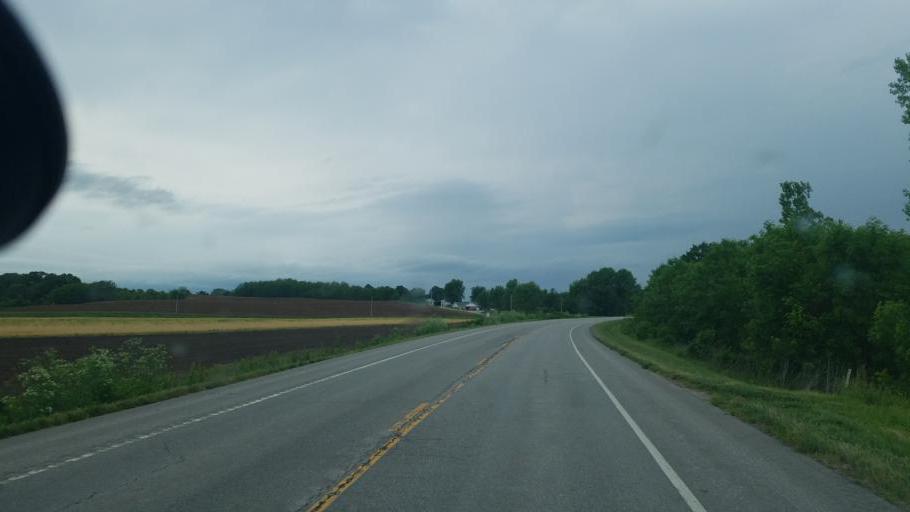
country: US
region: Missouri
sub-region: Cooper County
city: Boonville
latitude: 38.9013
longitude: -92.6711
